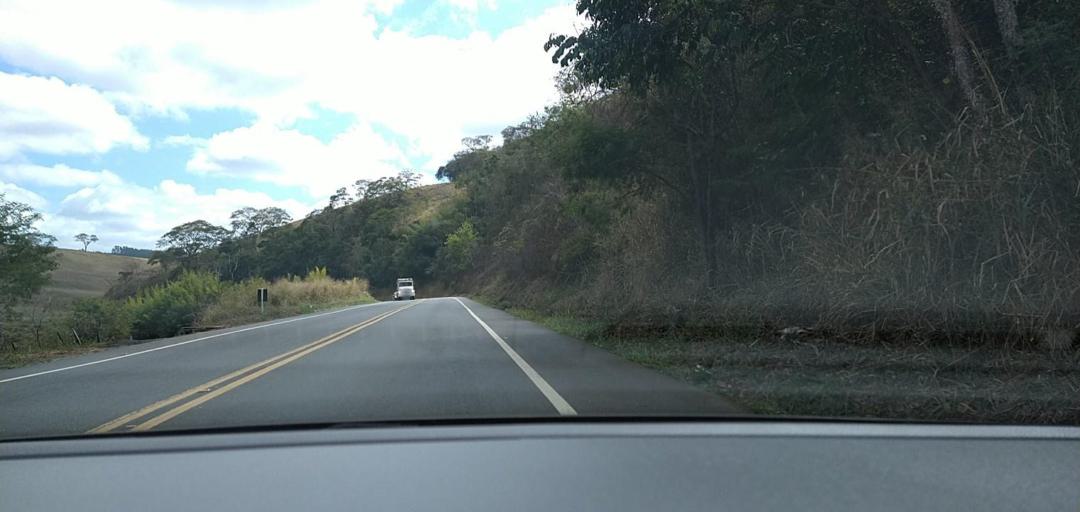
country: BR
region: Minas Gerais
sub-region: Ponte Nova
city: Ponte Nova
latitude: -20.4962
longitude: -42.8773
